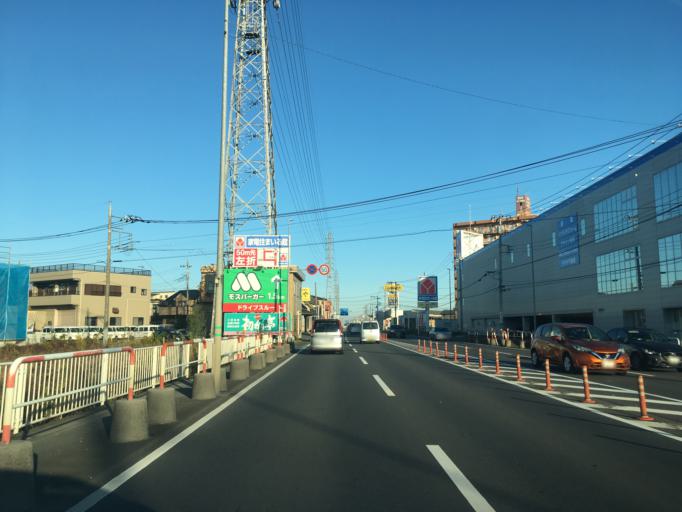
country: JP
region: Saitama
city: Kawagoe
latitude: 35.9299
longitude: 139.4903
